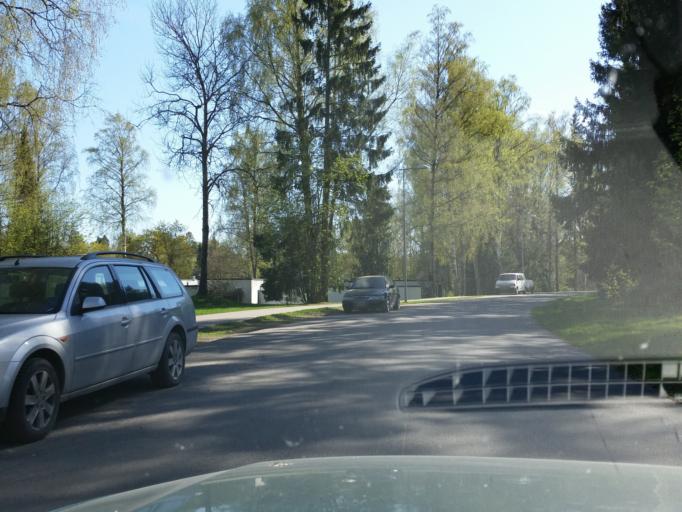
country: FI
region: Uusimaa
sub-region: Helsinki
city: Koukkuniemi
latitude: 60.1709
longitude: 24.7928
